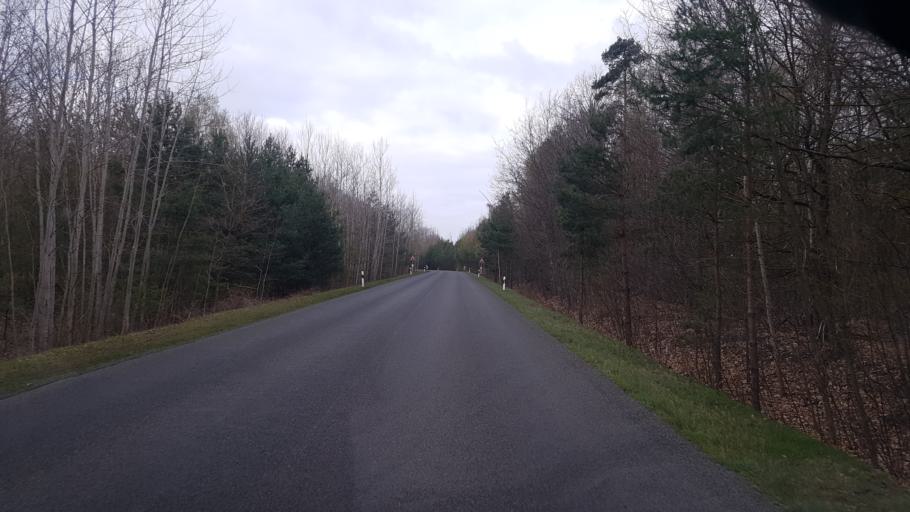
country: DE
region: Brandenburg
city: Lauchhammer
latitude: 51.4885
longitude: 13.7917
